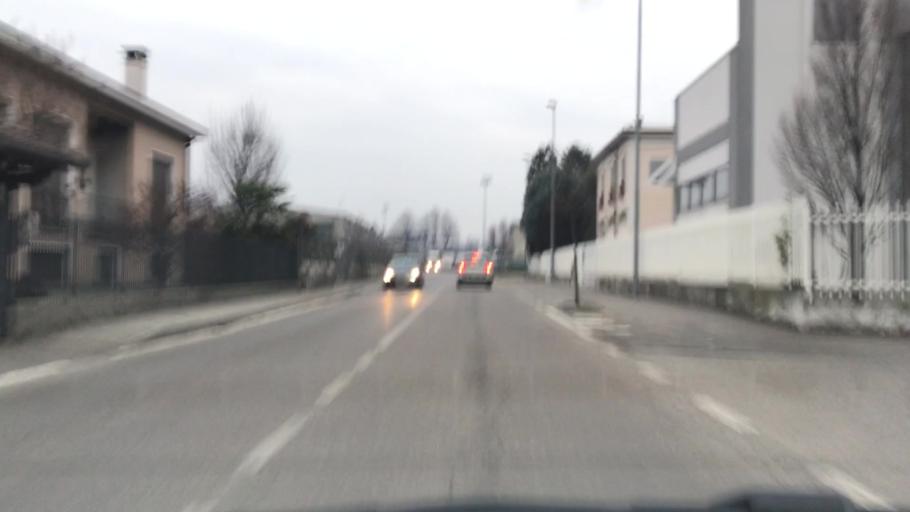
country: IT
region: Lombardy
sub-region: Provincia di Monza e Brianza
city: Seveso
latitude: 45.6507
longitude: 9.1484
